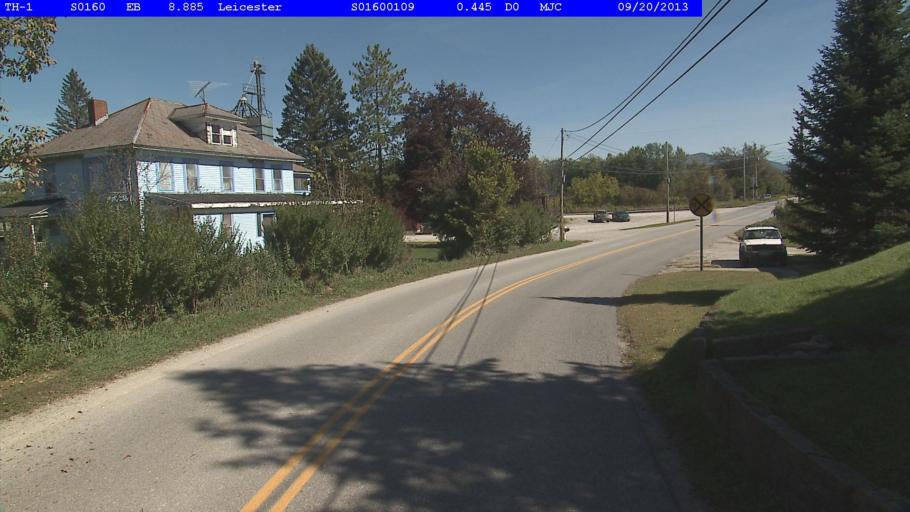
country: US
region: Vermont
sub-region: Rutland County
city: Brandon
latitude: 43.8557
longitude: -73.1510
